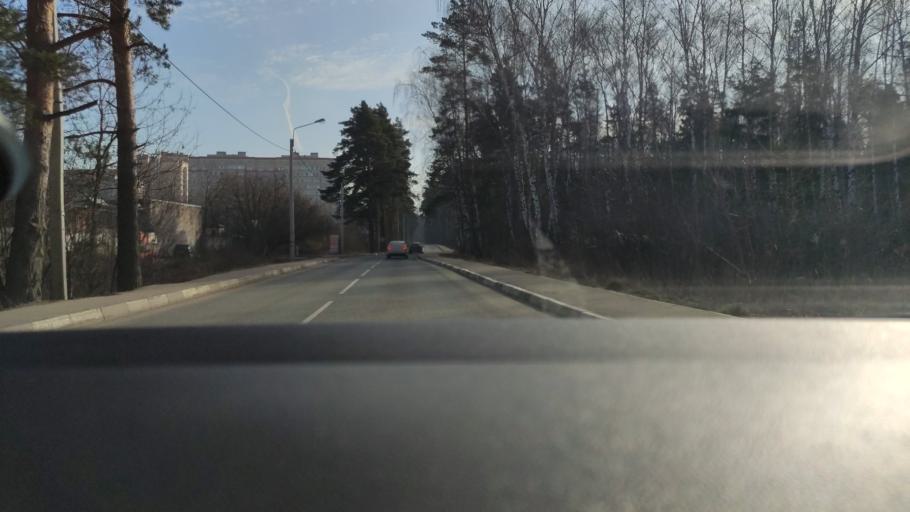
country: RU
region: Moskovskaya
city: Zarya
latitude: 55.8071
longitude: 38.0921
